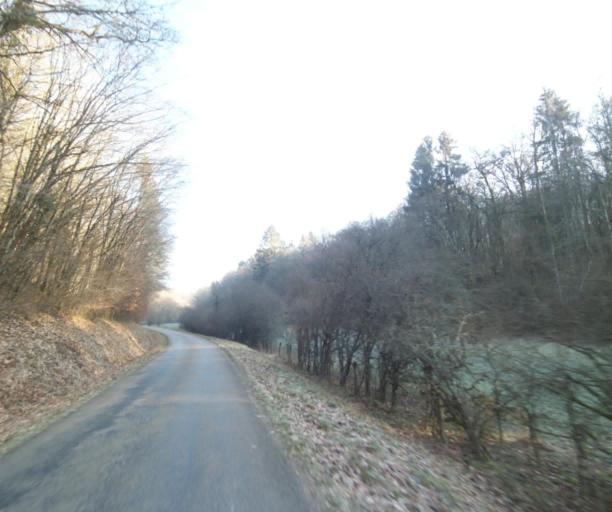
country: FR
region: Champagne-Ardenne
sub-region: Departement de la Haute-Marne
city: Joinville
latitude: 48.4896
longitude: 5.2276
